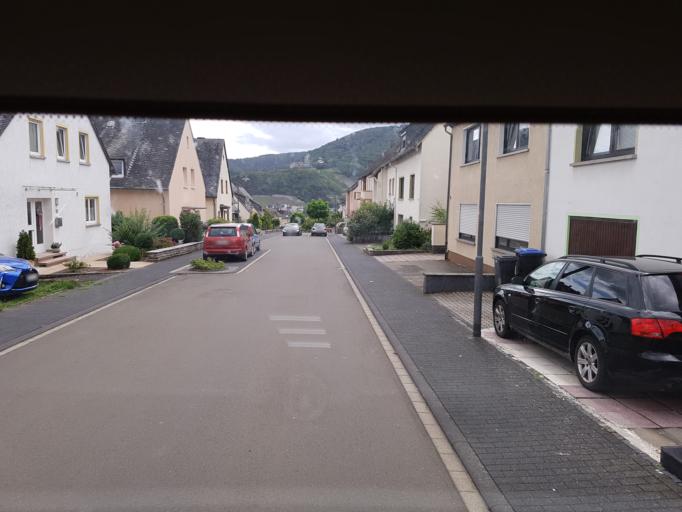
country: DE
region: Rheinland-Pfalz
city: Bernkastel-Kues
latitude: 49.9226
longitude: 7.0633
